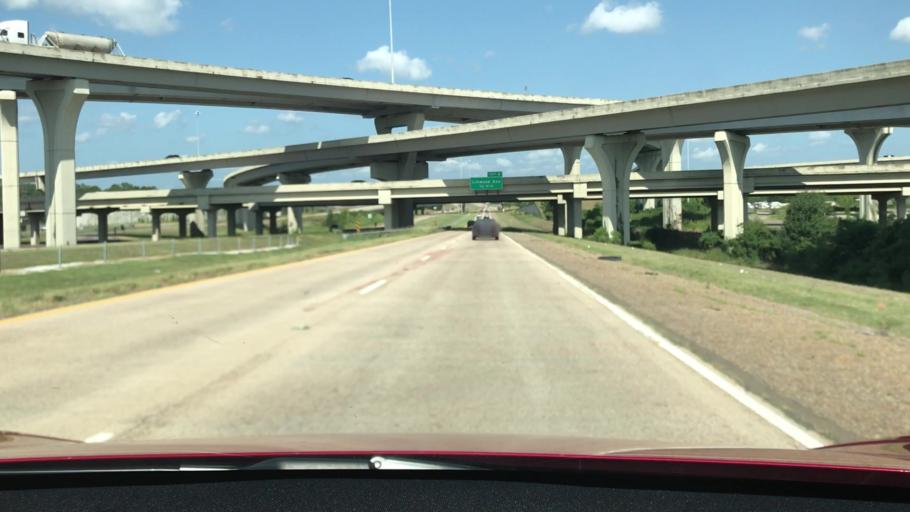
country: US
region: Louisiana
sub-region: Bossier Parish
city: Bossier City
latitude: 32.4190
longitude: -93.7481
